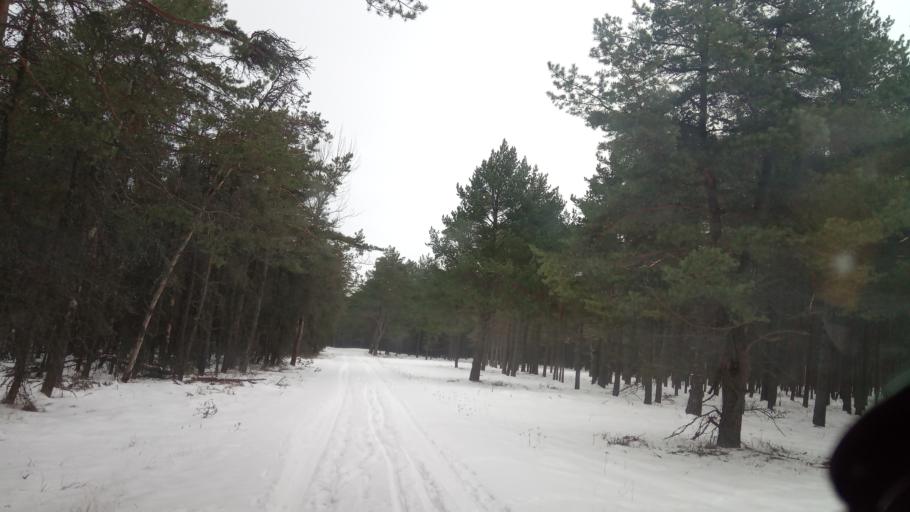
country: LT
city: Neringa
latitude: 55.4209
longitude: 21.0940
